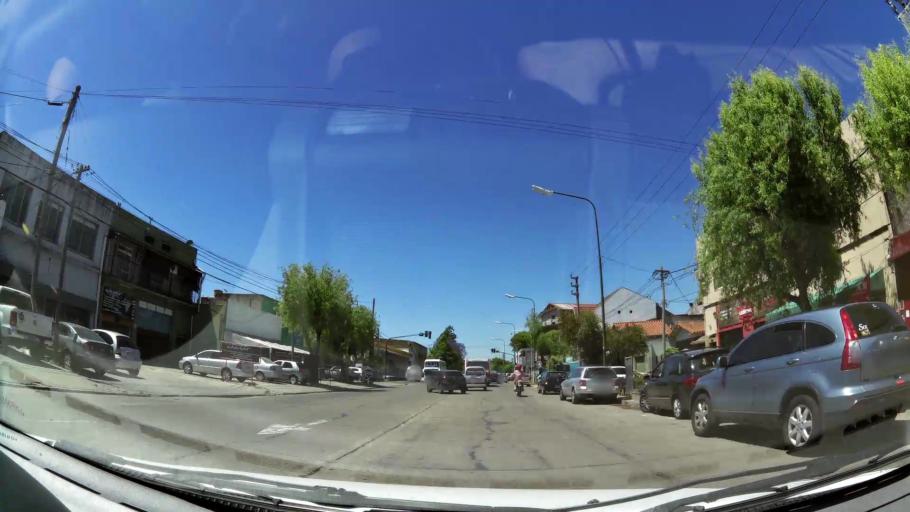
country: AR
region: Buenos Aires
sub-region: Partido de Vicente Lopez
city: Olivos
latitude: -34.5126
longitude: -58.5316
